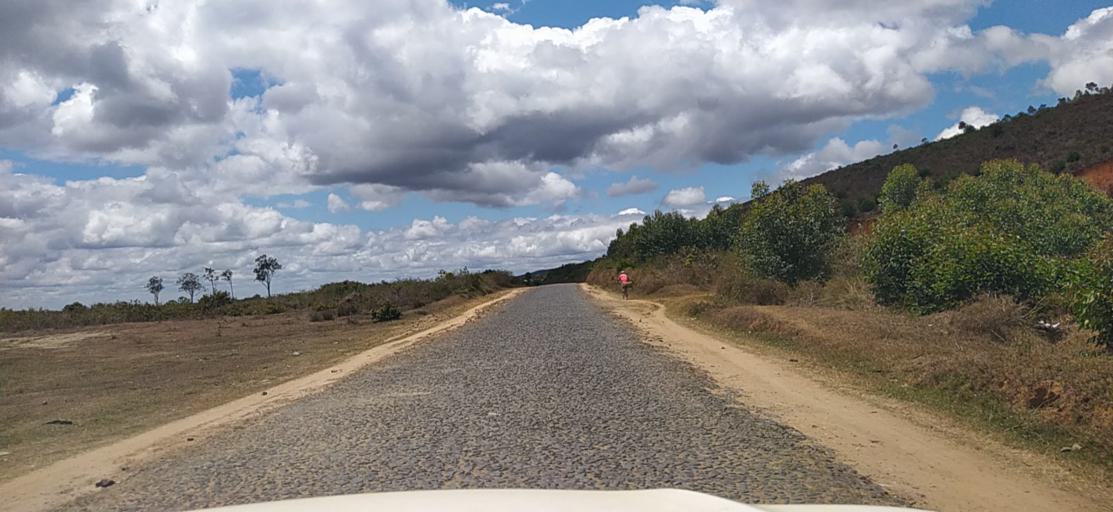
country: MG
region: Alaotra Mangoro
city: Moramanga
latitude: -18.7579
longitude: 48.2585
